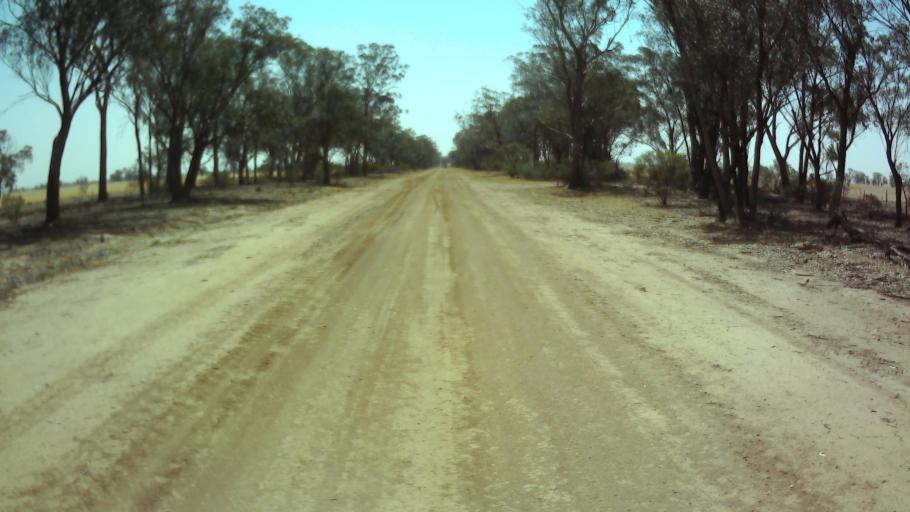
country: AU
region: New South Wales
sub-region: Weddin
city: Grenfell
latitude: -33.9269
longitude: 147.7907
